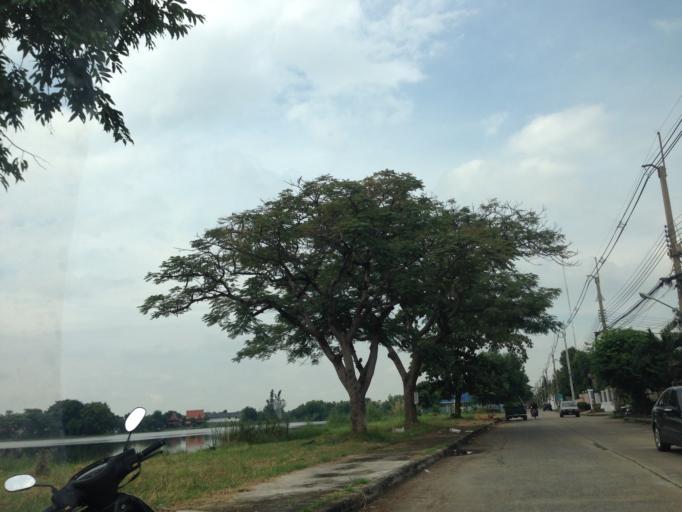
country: TH
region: Nonthaburi
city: Pak Kret
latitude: 13.9171
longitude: 100.5369
